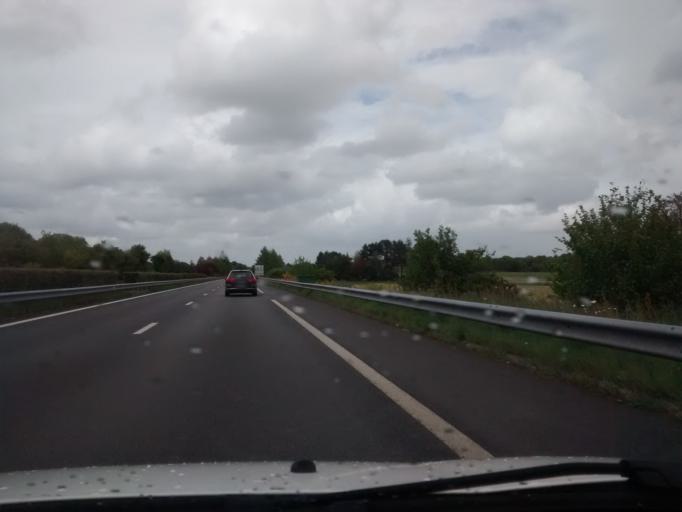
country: FR
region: Brittany
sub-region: Departement du Morbihan
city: Elven
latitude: 47.7135
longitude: -2.6106
